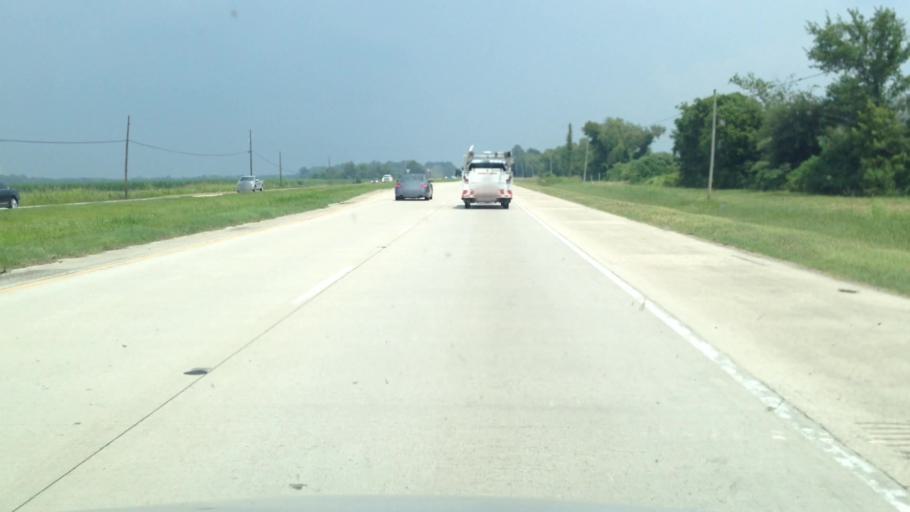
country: US
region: Louisiana
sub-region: West Baton Rouge Parish
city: Port Allen
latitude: 30.4938
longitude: -91.2912
